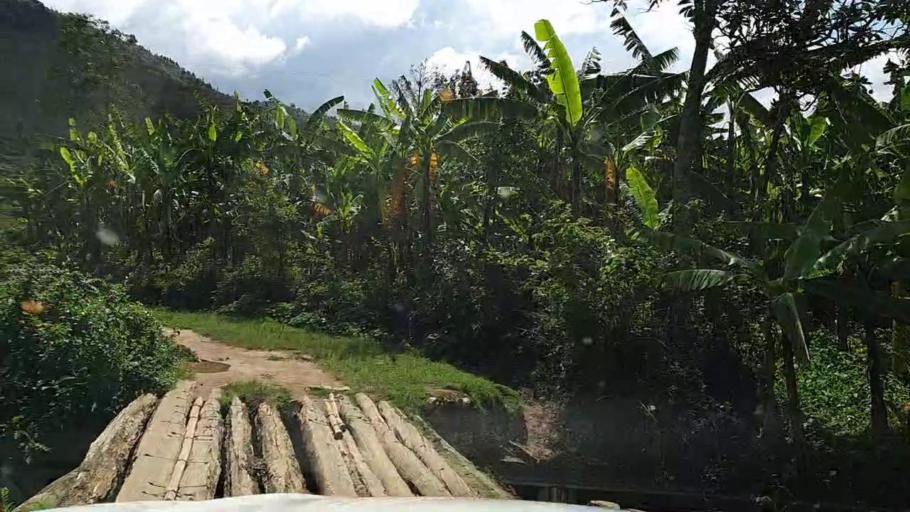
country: RW
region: Southern Province
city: Gikongoro
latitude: -2.3608
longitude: 29.5324
